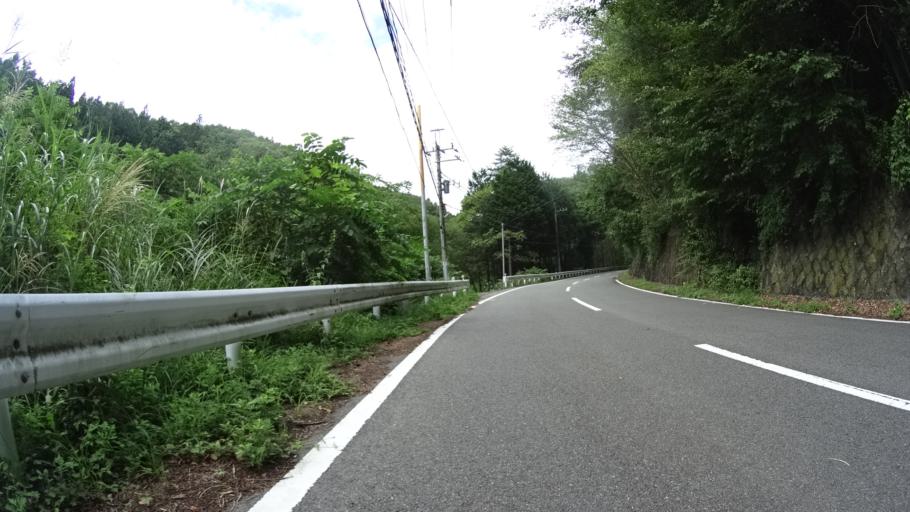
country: JP
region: Yamanashi
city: Kofu-shi
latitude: 35.7678
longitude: 138.5497
